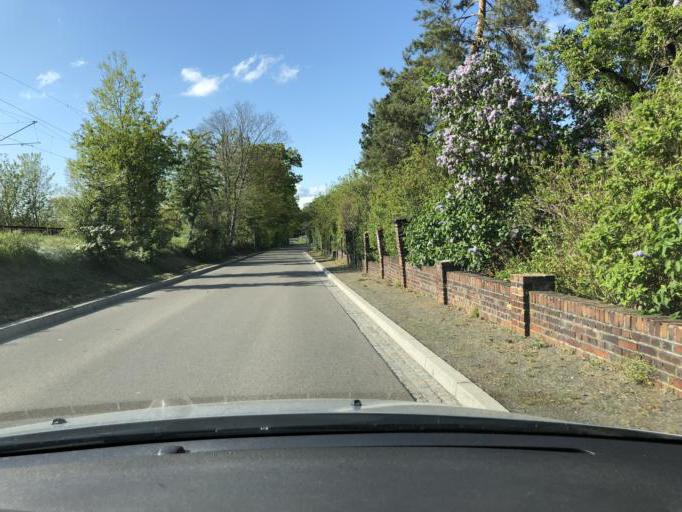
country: DE
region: Thuringia
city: Haselbach
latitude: 51.0551
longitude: 12.4387
